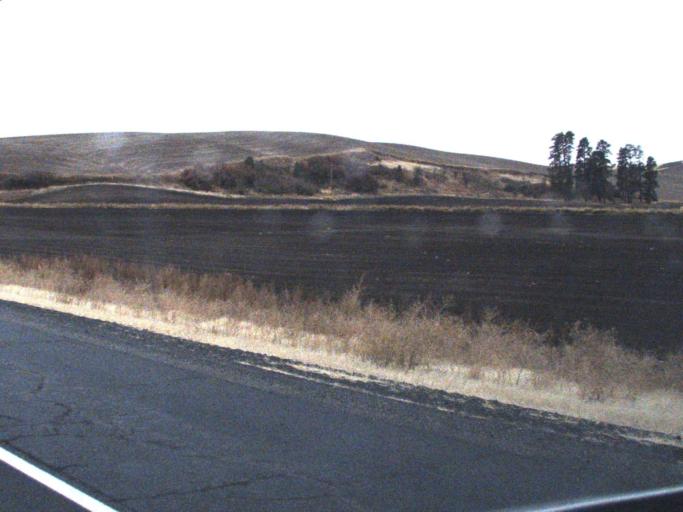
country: US
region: Washington
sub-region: Whitman County
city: Colfax
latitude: 46.9537
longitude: -117.3336
